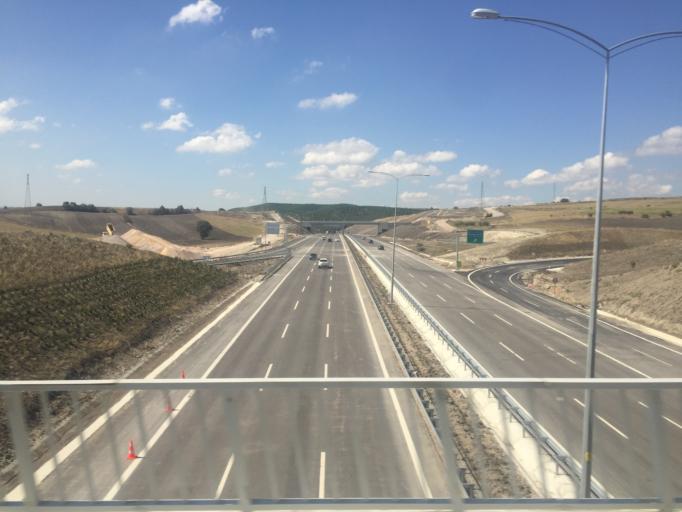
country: TR
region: Balikesir
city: Gobel
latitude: 39.9690
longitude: 28.1616
